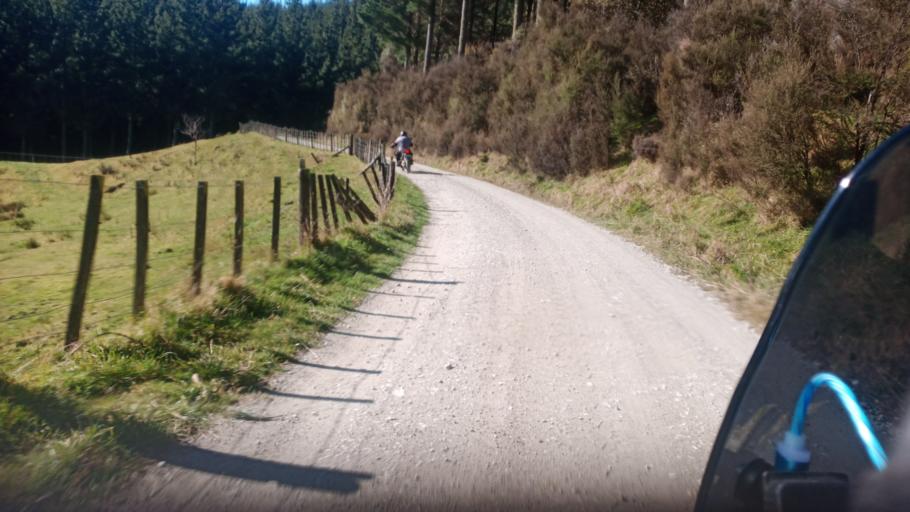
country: NZ
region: Hawke's Bay
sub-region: Wairoa District
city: Wairoa
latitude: -38.6574
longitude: 177.4917
